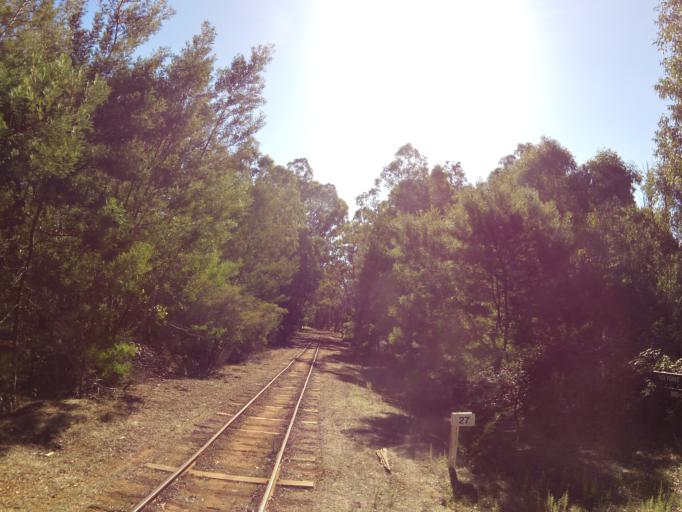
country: AU
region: Western Australia
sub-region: Waroona
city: Waroona
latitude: -32.7144
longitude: 116.0933
